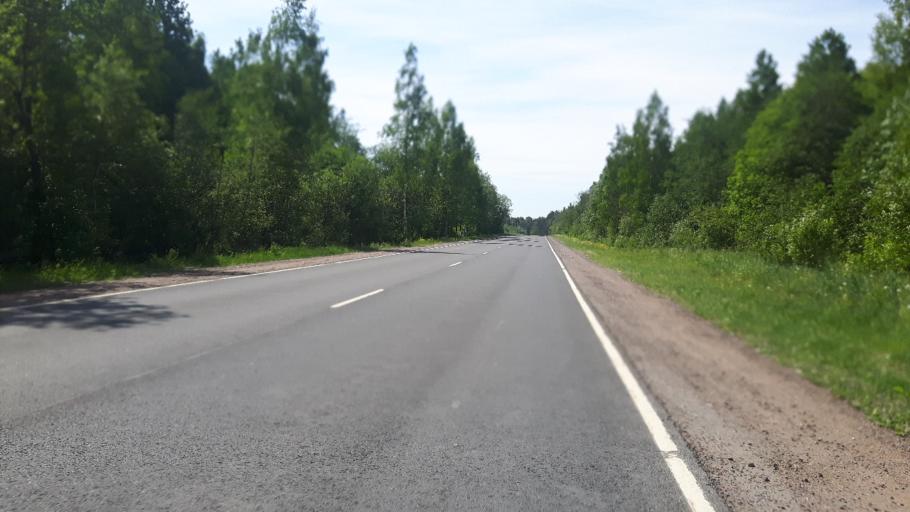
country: RU
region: Leningrad
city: Vistino
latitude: 59.6768
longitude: 28.4528
